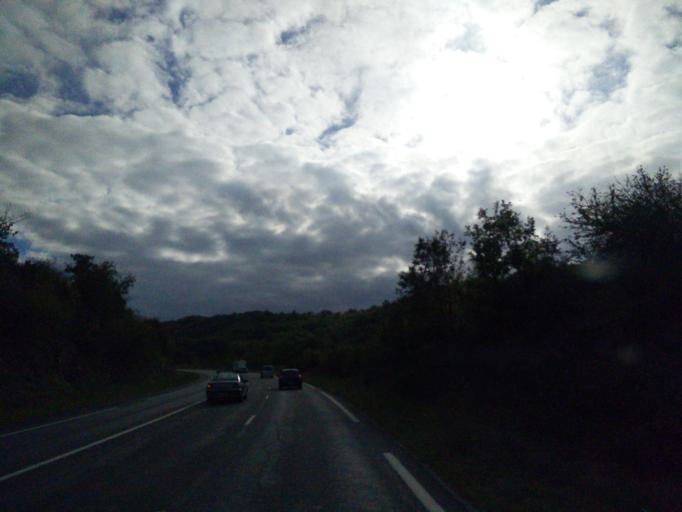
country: FR
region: Midi-Pyrenees
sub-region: Departement du Lot
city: Cahors
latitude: 44.4580
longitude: 1.4133
